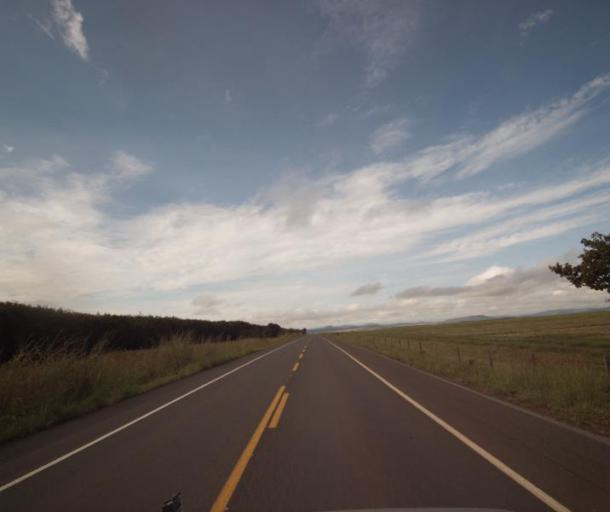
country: BR
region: Goias
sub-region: Padre Bernardo
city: Padre Bernardo
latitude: -15.3720
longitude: -48.6457
